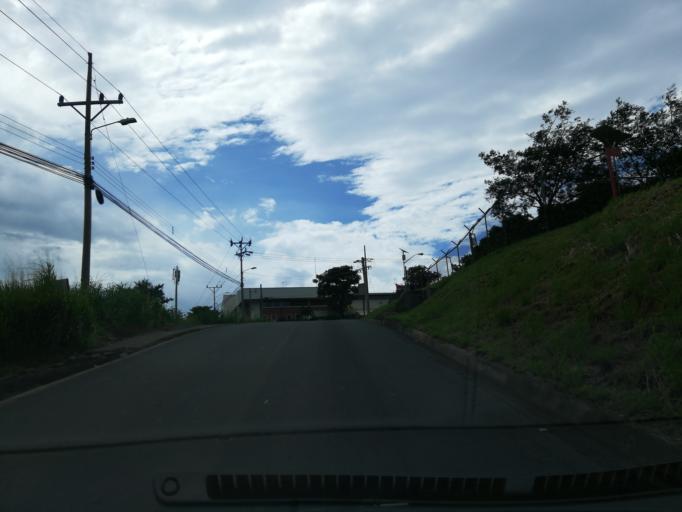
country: CR
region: Alajuela
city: Alajuela
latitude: 9.9979
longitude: -84.2137
